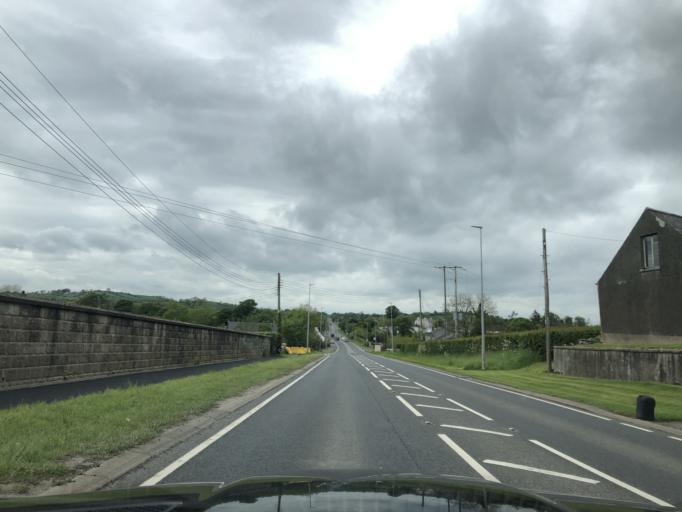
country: GB
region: Northern Ireland
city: Crossgar
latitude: 54.3622
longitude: -5.7678
